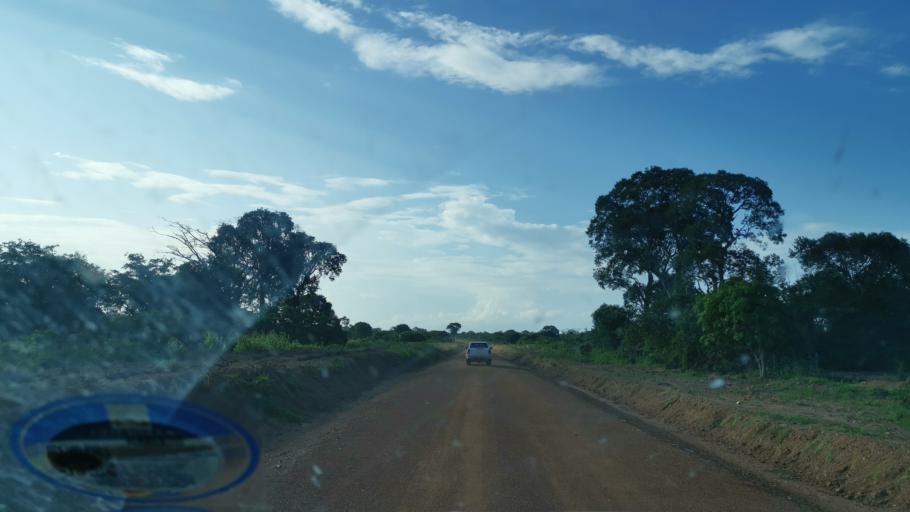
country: ZM
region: Luapula
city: Samfya
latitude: -11.1100
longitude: 29.5758
